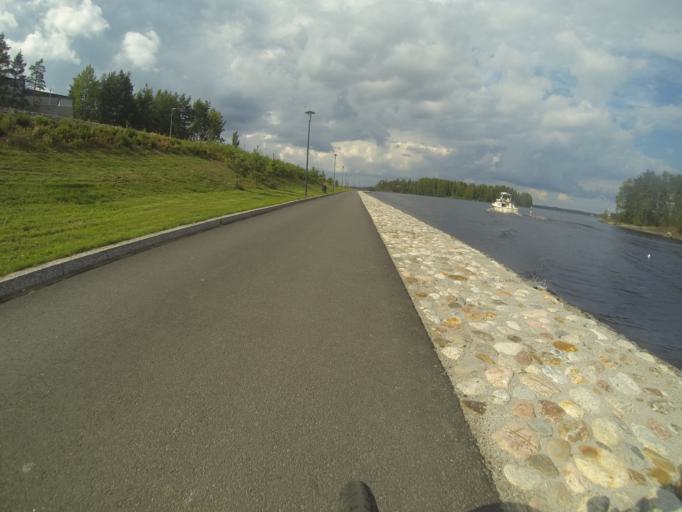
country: FI
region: Southern Savonia
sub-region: Savonlinna
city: Savonlinna
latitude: 61.8722
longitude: 28.8822
